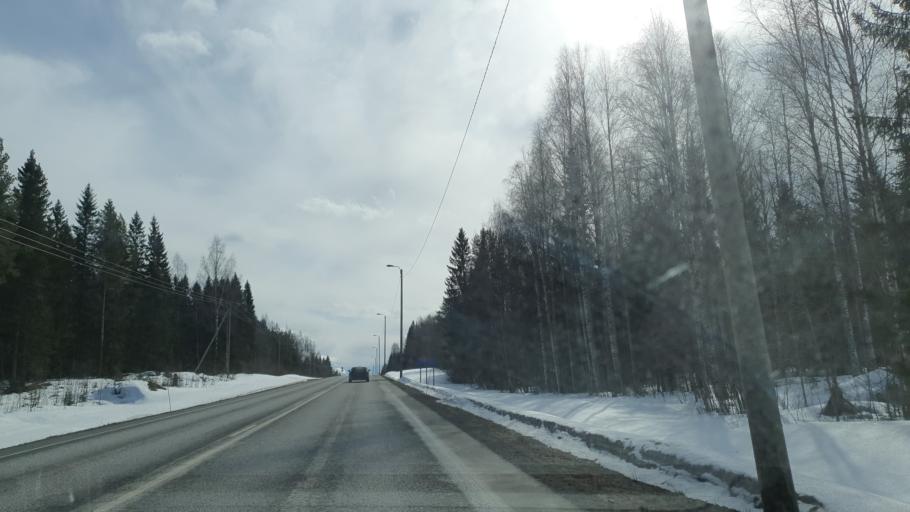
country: FI
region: Kainuu
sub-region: Kajaani
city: Ristijaervi
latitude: 64.3476
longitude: 28.0528
